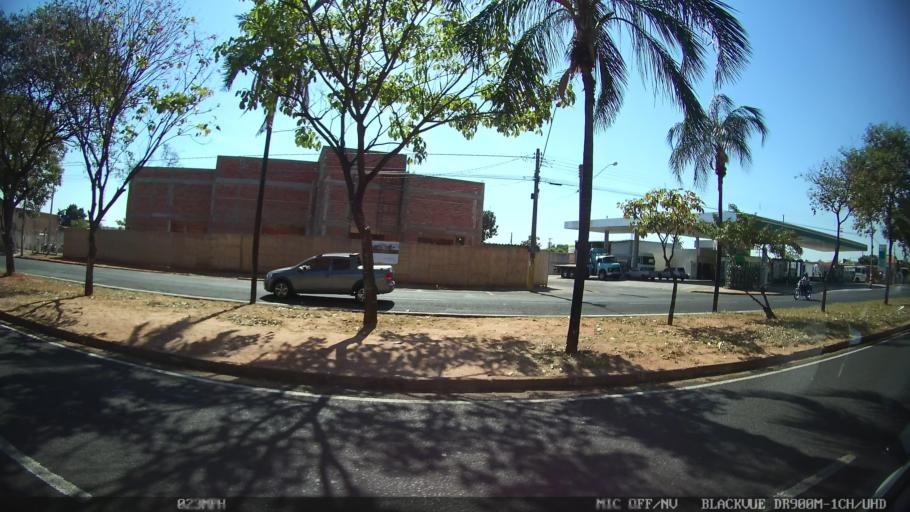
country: BR
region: Sao Paulo
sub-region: Sao Jose Do Rio Preto
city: Sao Jose do Rio Preto
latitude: -20.7796
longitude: -49.3711
